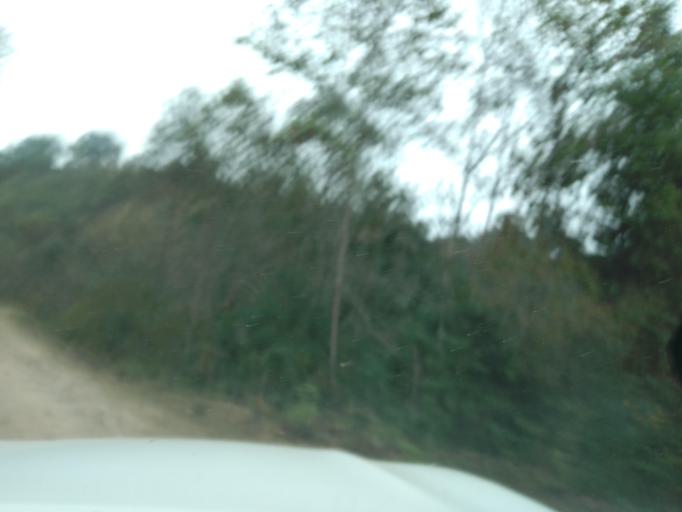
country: MX
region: Chiapas
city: Motozintla de Mendoza
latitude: 15.2184
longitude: -92.2209
